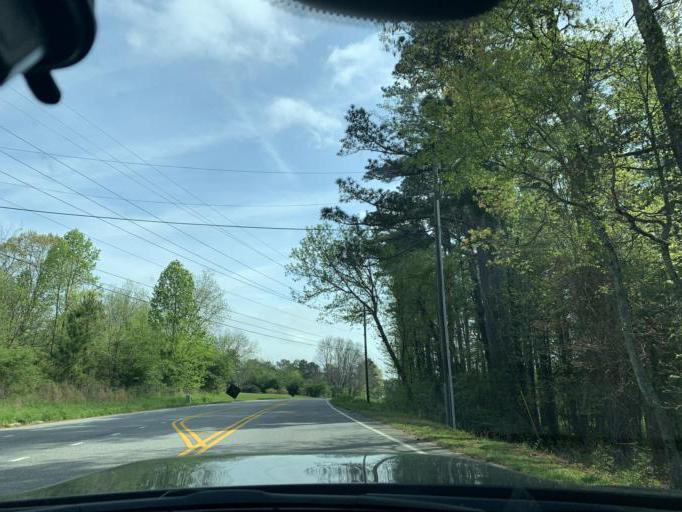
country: US
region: Georgia
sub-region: Forsyth County
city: Cumming
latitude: 34.2482
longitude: -84.0800
